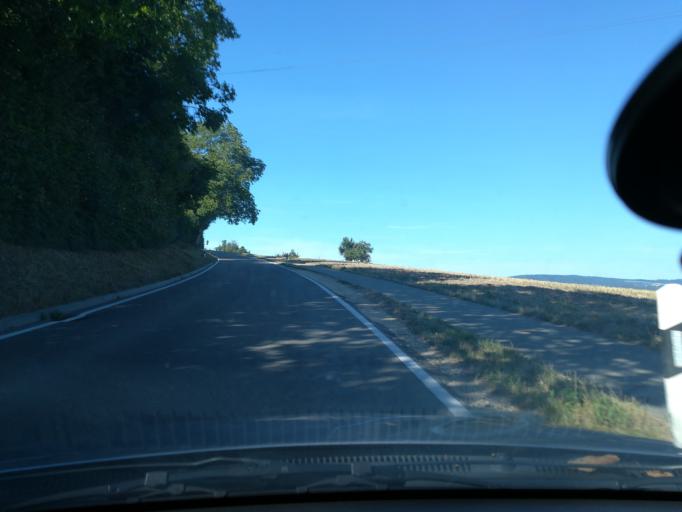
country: DE
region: Baden-Wuerttemberg
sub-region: Freiburg Region
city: Moos
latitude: 47.7245
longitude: 8.9014
